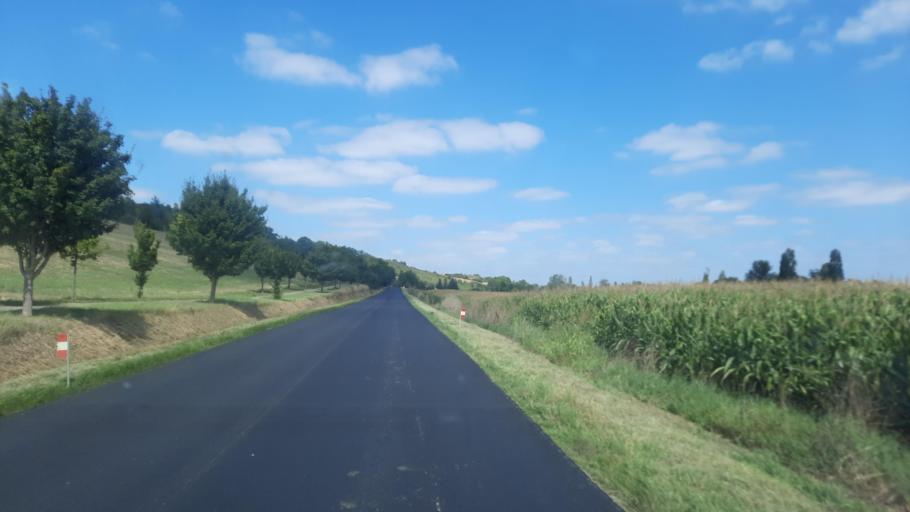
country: FR
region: Midi-Pyrenees
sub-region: Departement du Gers
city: Lombez
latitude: 43.4657
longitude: 0.8918
